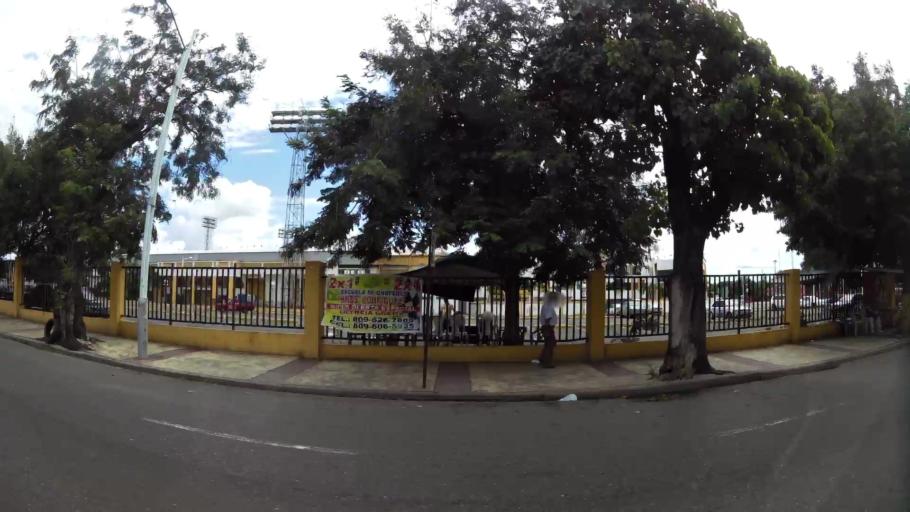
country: DO
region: Santiago
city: Santiago de los Caballeros
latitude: 19.4673
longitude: -70.7103
